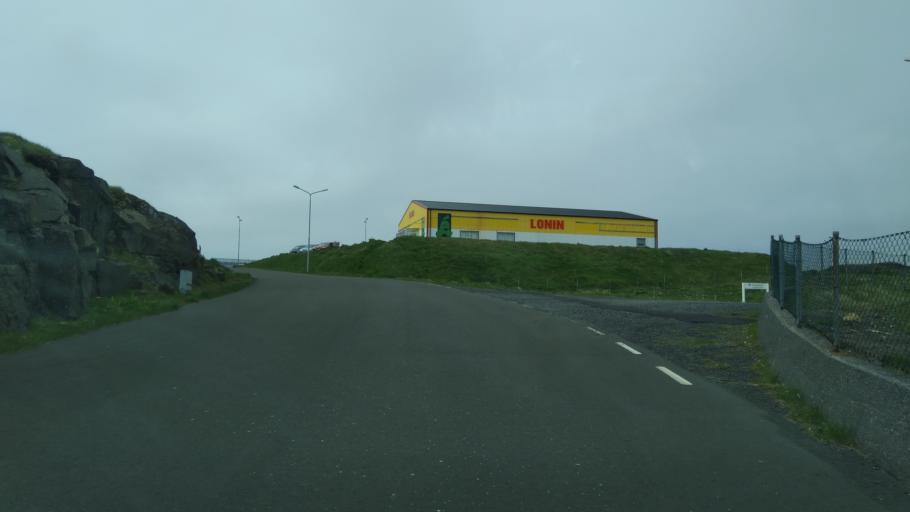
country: FO
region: Sandoy
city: Sandur
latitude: 61.9047
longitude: -6.8837
